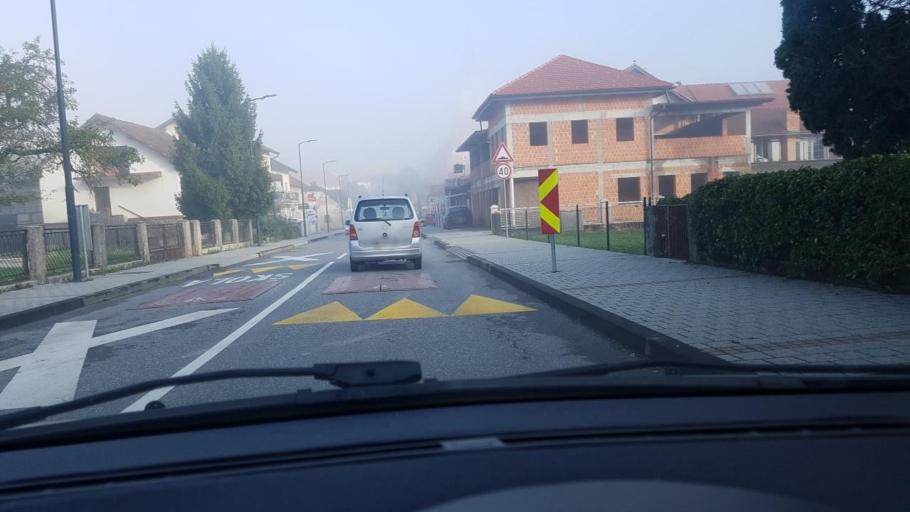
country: HR
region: Krapinsko-Zagorska
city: Marija Bistrica
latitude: 46.0023
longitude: 16.1193
